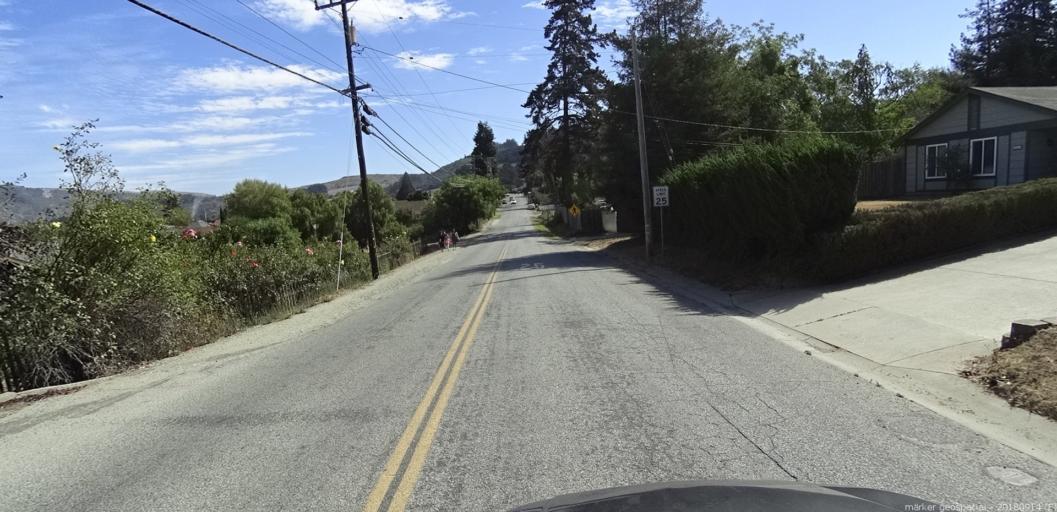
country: US
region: California
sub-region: San Benito County
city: Aromas
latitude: 36.8881
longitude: -121.6470
